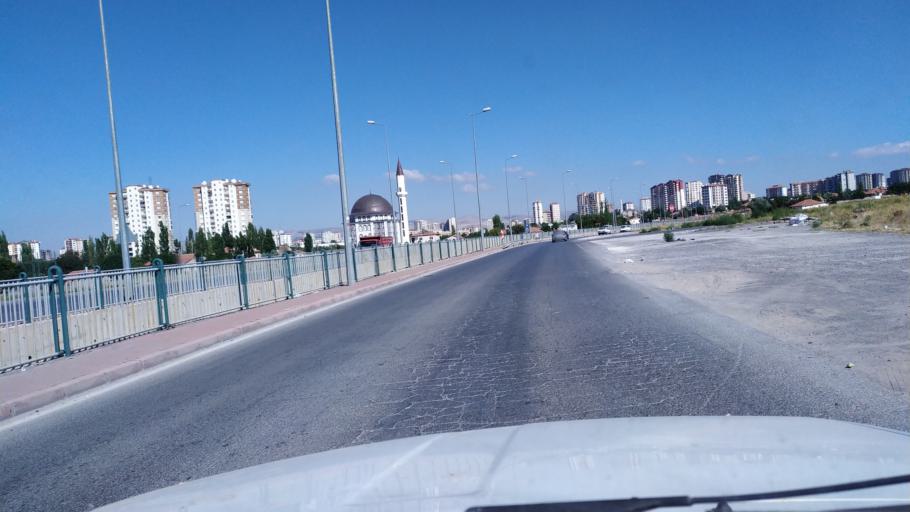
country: TR
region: Kayseri
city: Talas
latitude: 38.7295
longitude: 35.5498
